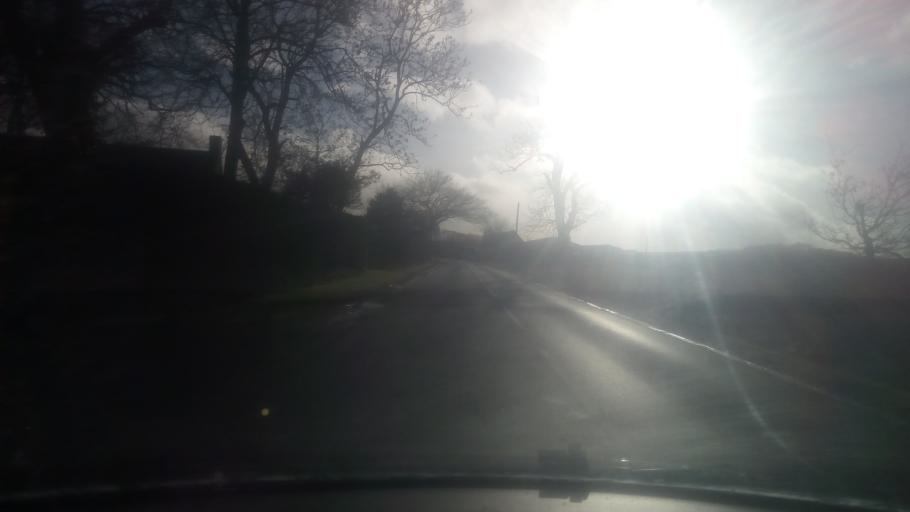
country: GB
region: Scotland
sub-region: The Scottish Borders
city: Kelso
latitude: 55.6682
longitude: -2.3736
